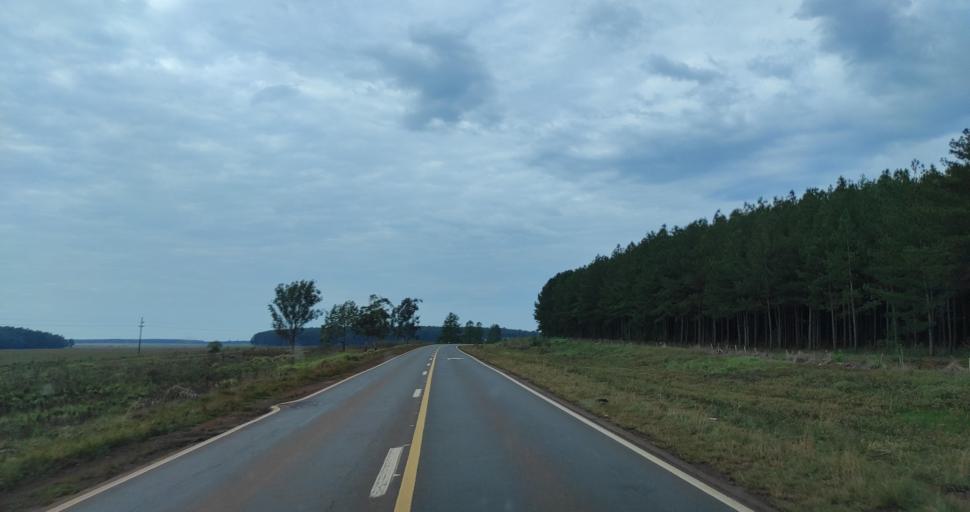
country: AR
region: Corrientes
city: Gobernador Ingeniero Valentin Virasoro
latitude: -28.2501
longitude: -56.1029
